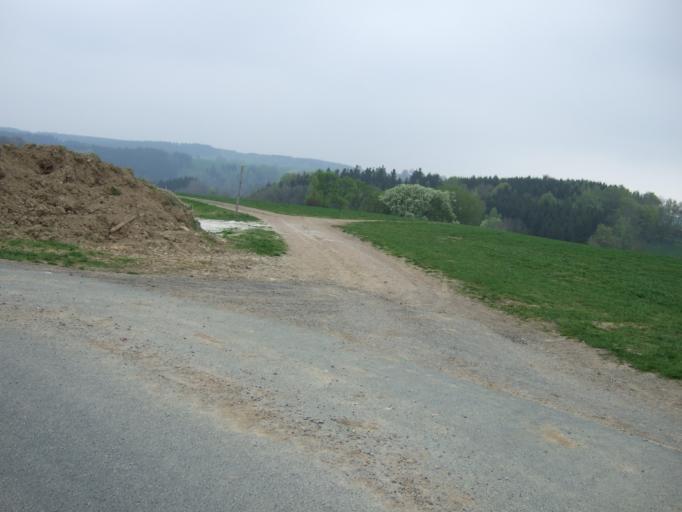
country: DE
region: Saxony
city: Rechenberg-Bienenmuhle
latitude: 50.7602
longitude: 13.5226
